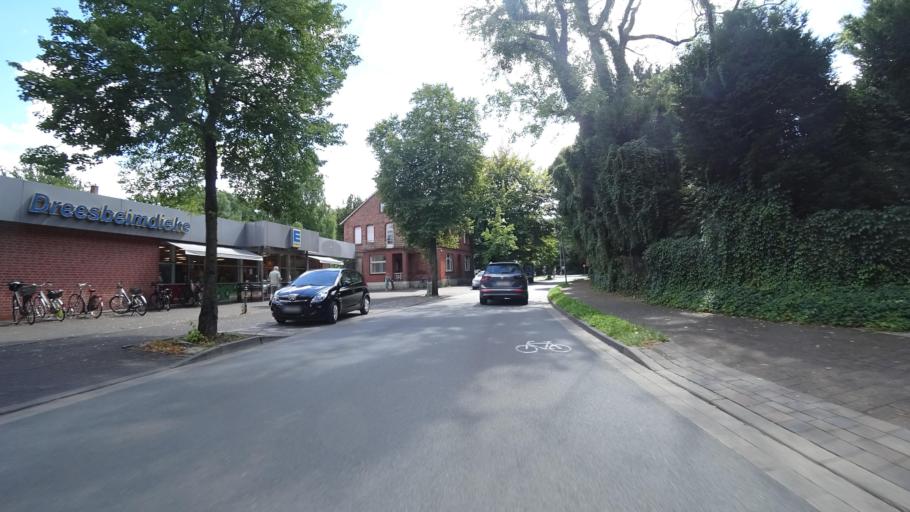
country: DE
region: North Rhine-Westphalia
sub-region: Regierungsbezirk Detmold
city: Guetersloh
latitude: 51.9455
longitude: 8.4119
